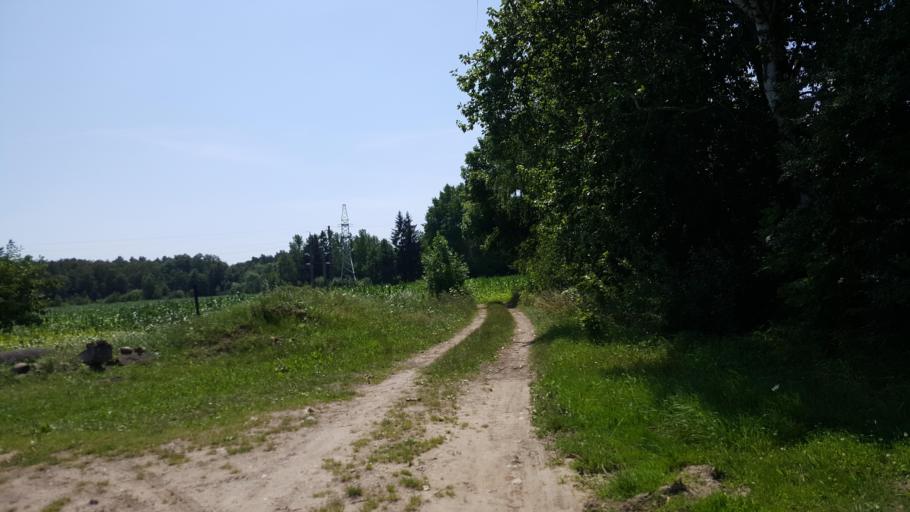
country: BY
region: Brest
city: Vysokaye
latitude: 52.3590
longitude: 23.4016
